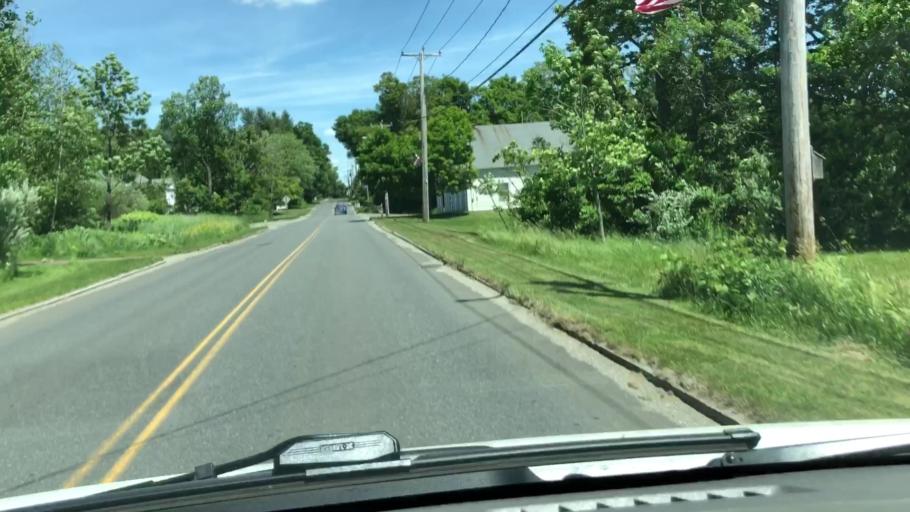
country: US
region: Massachusetts
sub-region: Franklin County
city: Charlemont
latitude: 42.5162
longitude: -72.9138
